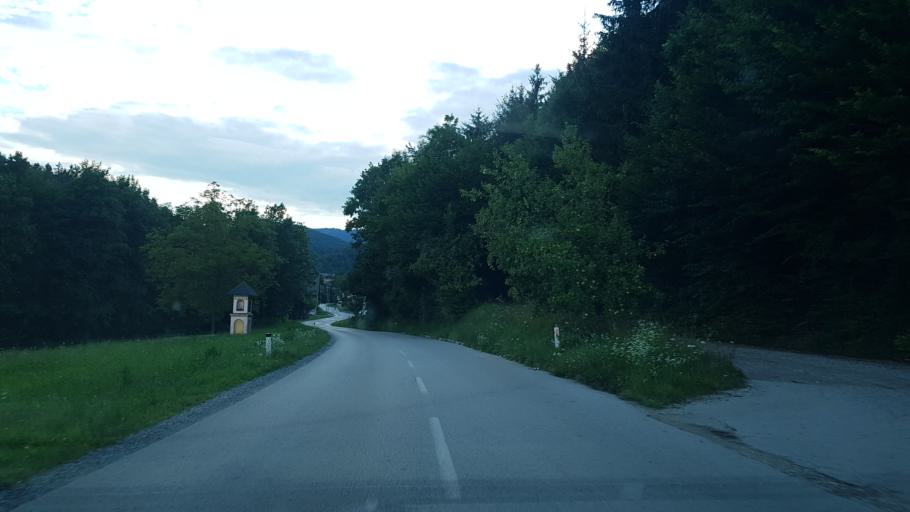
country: SI
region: Naklo
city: Naklo
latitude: 46.2610
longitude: 14.2887
